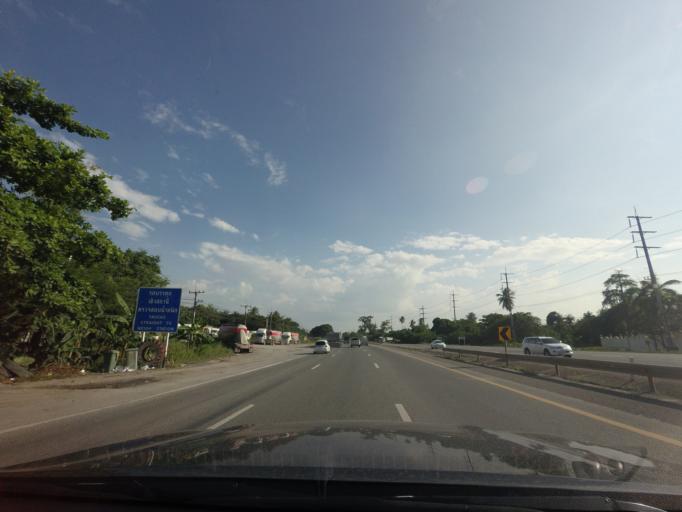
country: TH
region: Sara Buri
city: Chaloem Phra Kiat
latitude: 14.6514
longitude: 100.8845
